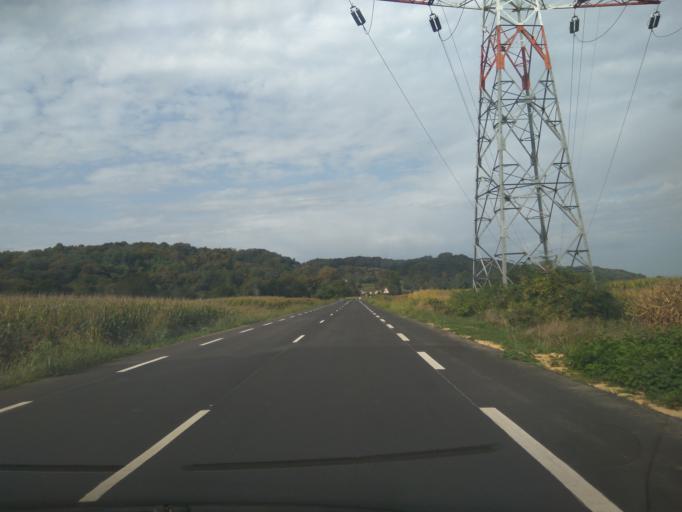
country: FR
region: Aquitaine
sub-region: Departement des Pyrenees-Atlantiques
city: Arbus
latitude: 43.3378
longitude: -0.5026
